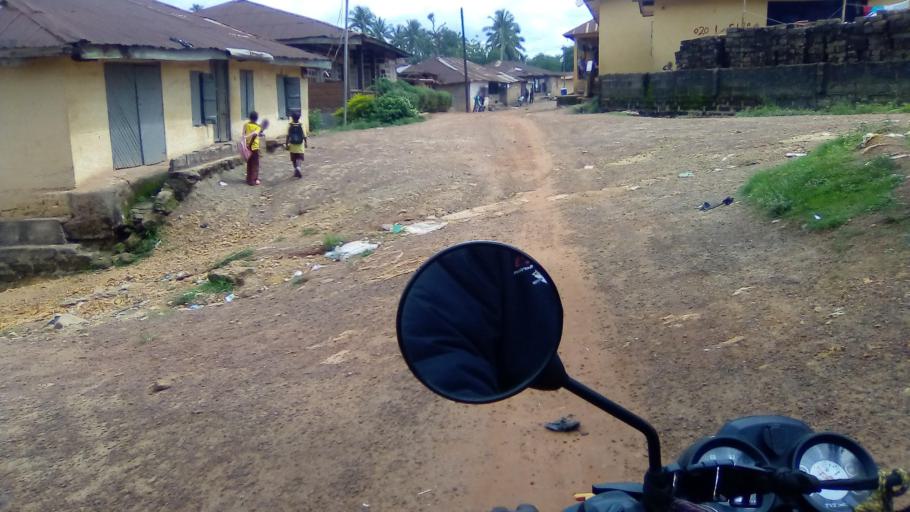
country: SL
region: Southern Province
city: Bo
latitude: 7.9612
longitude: -11.7306
